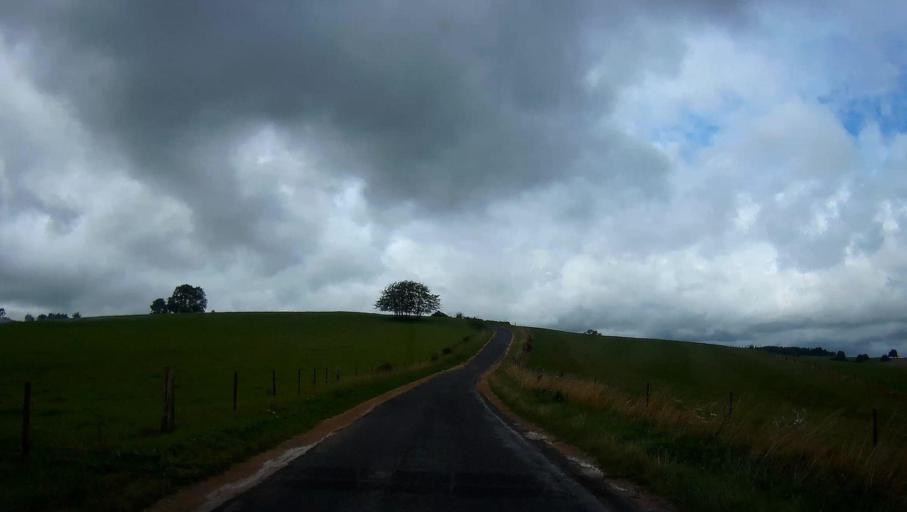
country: FR
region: Champagne-Ardenne
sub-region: Departement des Ardennes
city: Rimogne
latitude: 49.7594
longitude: 4.5200
